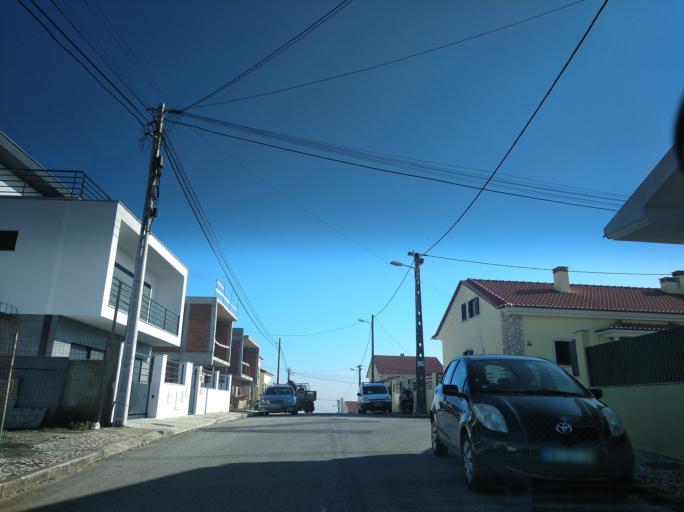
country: PT
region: Lisbon
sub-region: Odivelas
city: Canecas
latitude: 38.8026
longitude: -9.2202
